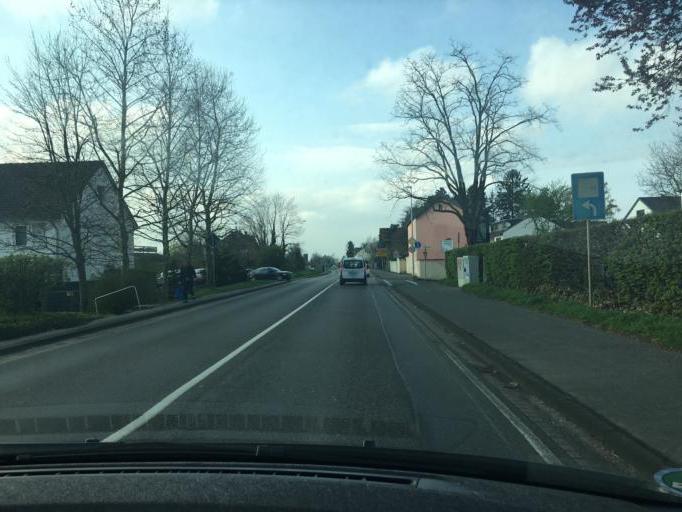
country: DE
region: North Rhine-Westphalia
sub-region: Regierungsbezirk Koln
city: Alfter
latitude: 50.7691
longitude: 7.0451
